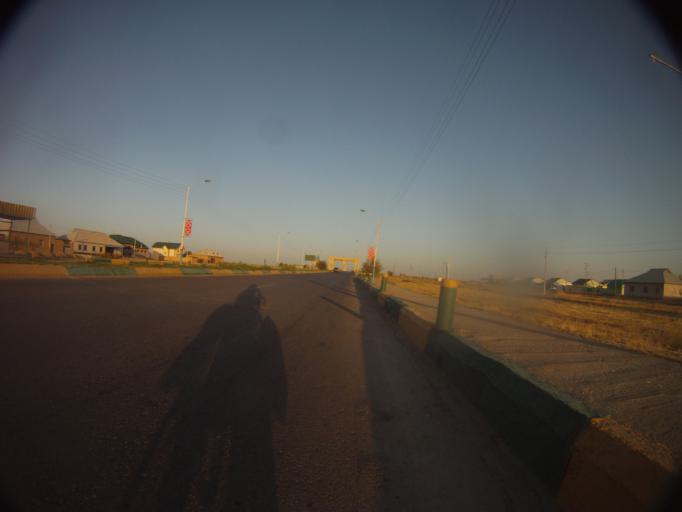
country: KZ
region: Ongtustik Qazaqstan
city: Turkestan
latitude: 43.2779
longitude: 68.3278
